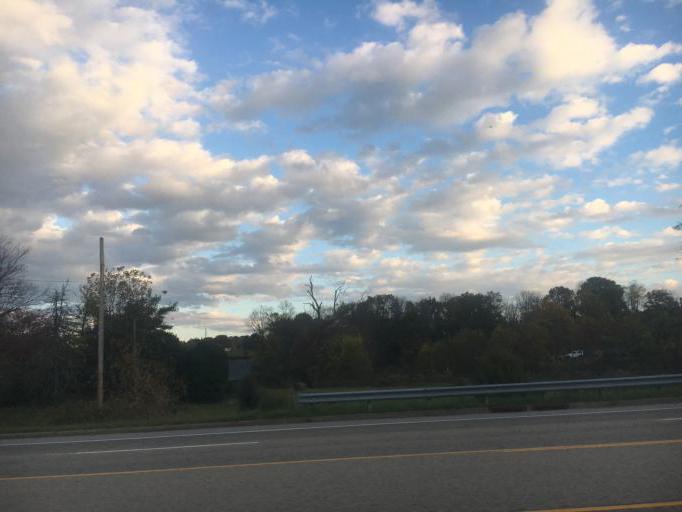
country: US
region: Tennessee
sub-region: Washington County
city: Gray
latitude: 36.4196
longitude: -82.4678
